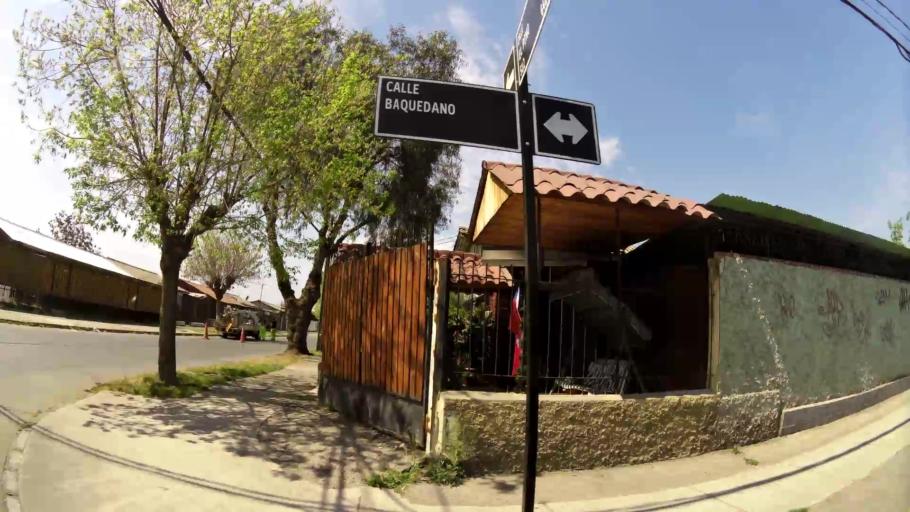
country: CL
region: Santiago Metropolitan
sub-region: Provincia de Santiago
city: La Pintana
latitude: -33.5511
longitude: -70.6653
